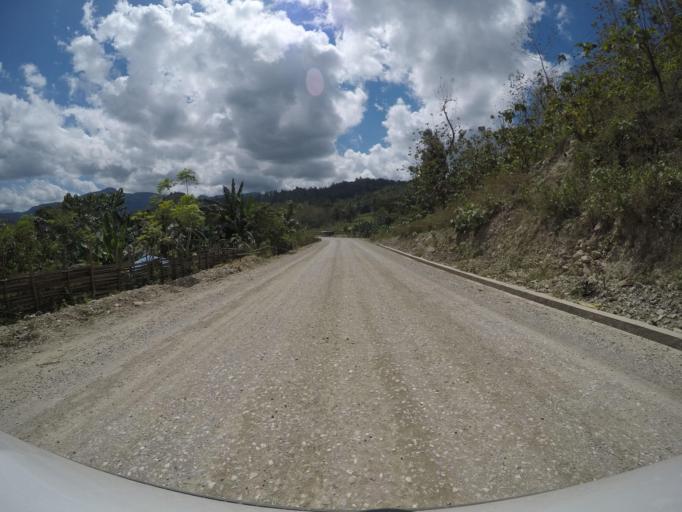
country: TL
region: Viqueque
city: Viqueque
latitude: -8.8283
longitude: 126.3759
